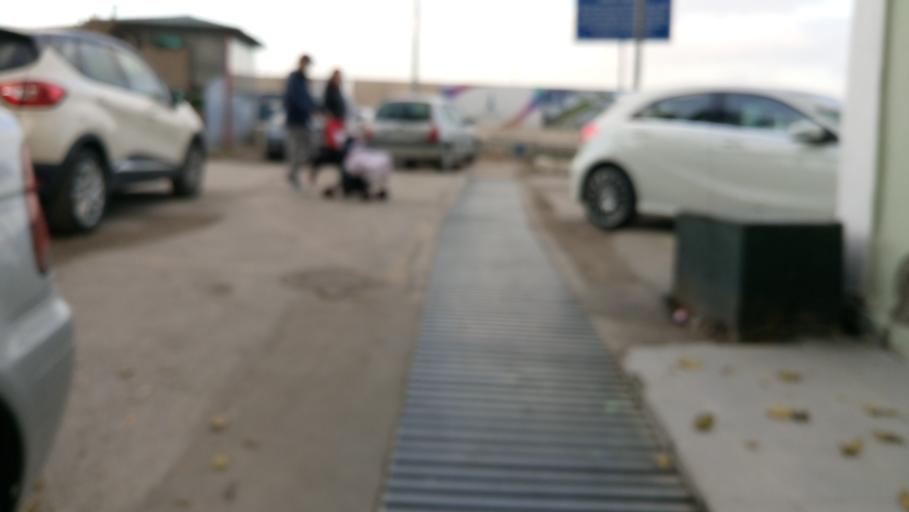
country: TR
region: Izmir
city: Izmir
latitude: 38.4071
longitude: 27.1034
